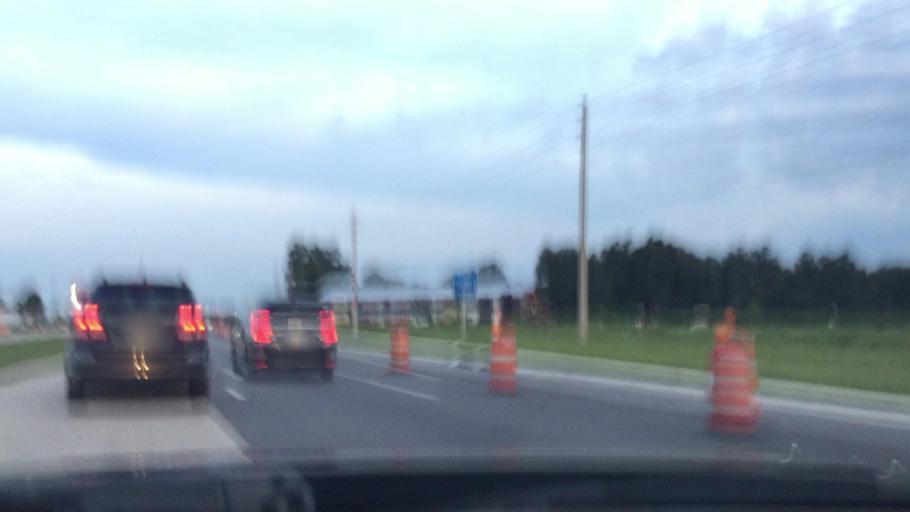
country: US
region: Florida
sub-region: Osceola County
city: Buenaventura Lakes
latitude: 28.2787
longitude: -81.3433
